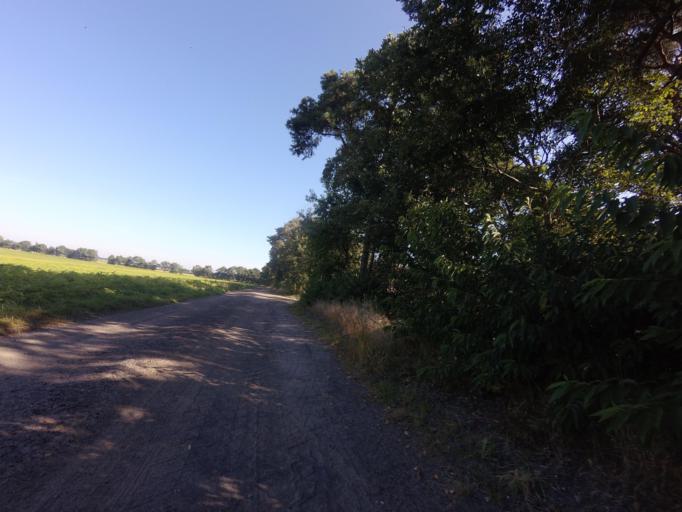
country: DE
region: Lower Saxony
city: Wielen
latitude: 52.5476
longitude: 6.7054
